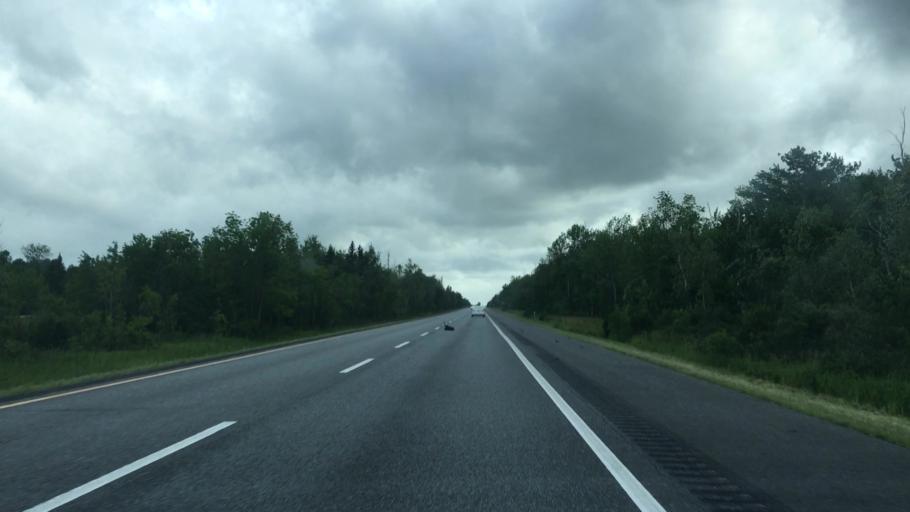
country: US
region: Maine
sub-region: Waldo County
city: Burnham
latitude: 44.6875
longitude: -69.4739
